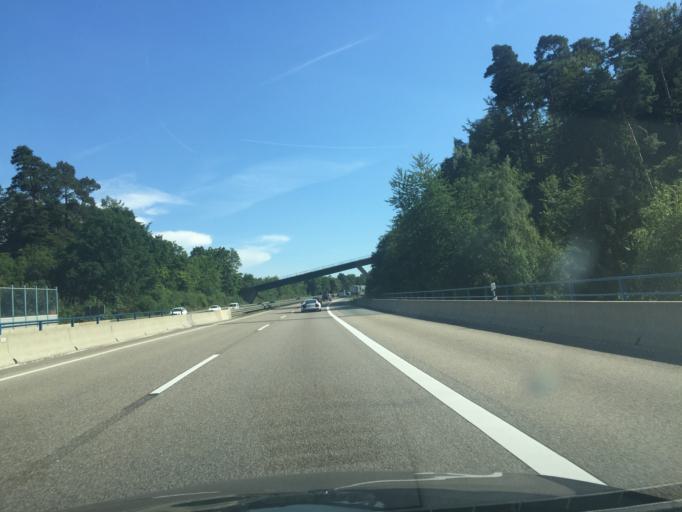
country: DE
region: Hesse
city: Herborn
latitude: 50.6962
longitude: 8.2936
